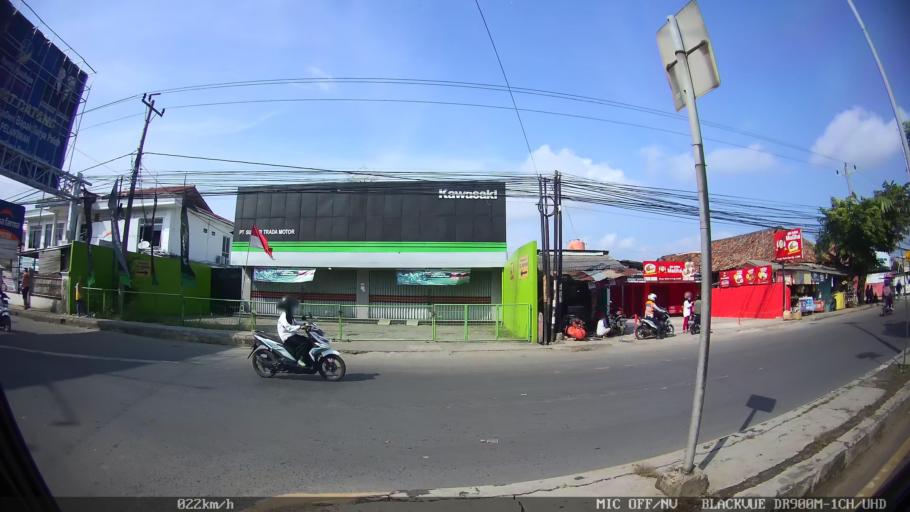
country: ID
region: Lampung
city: Kedaton
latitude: -5.3740
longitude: 105.2421
